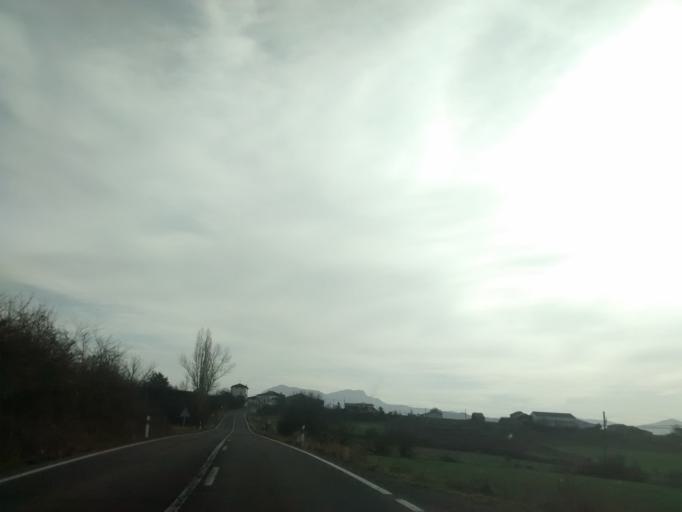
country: ES
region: Aragon
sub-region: Provincia de Zaragoza
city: Mianos
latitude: 42.6015
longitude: -0.8636
